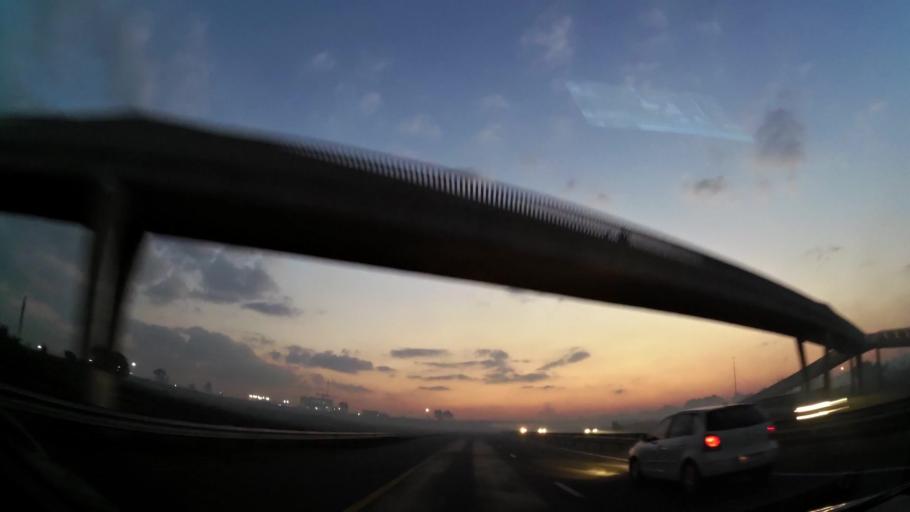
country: ZA
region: Gauteng
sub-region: Ekurhuleni Metropolitan Municipality
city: Springs
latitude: -26.2758
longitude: 28.3812
